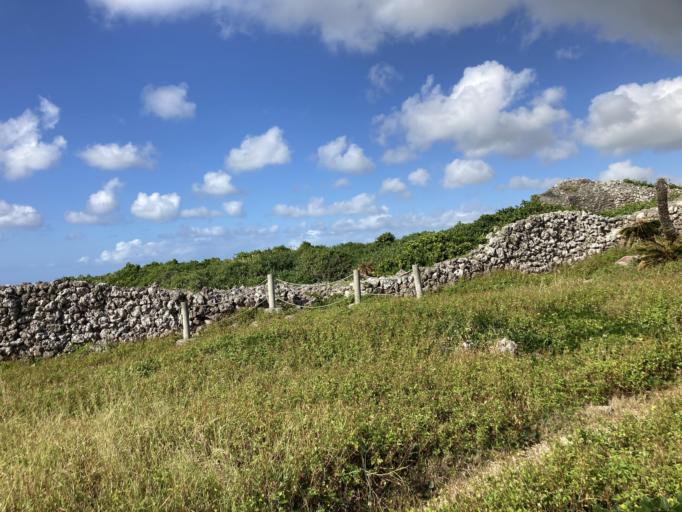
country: JP
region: Okinawa
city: Itoman
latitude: 26.0801
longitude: 127.6642
